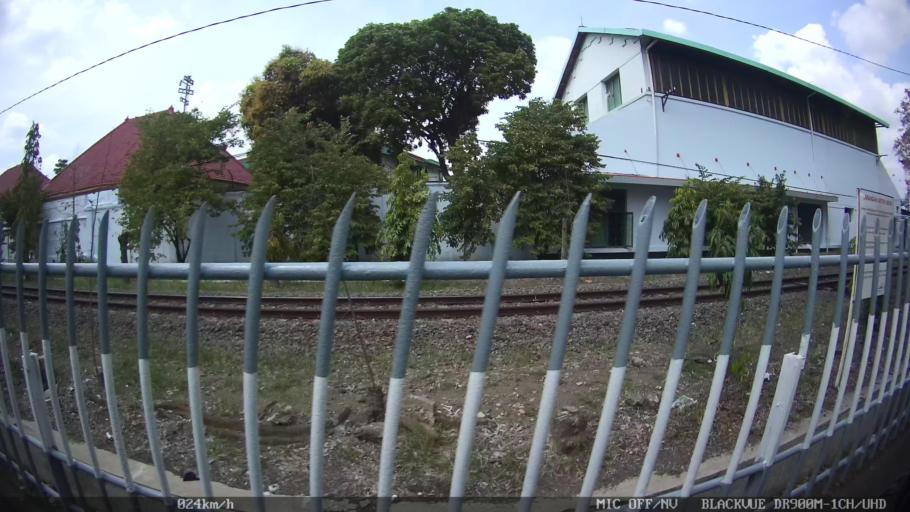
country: ID
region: Daerah Istimewa Yogyakarta
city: Yogyakarta
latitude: -7.7871
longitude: 110.3833
